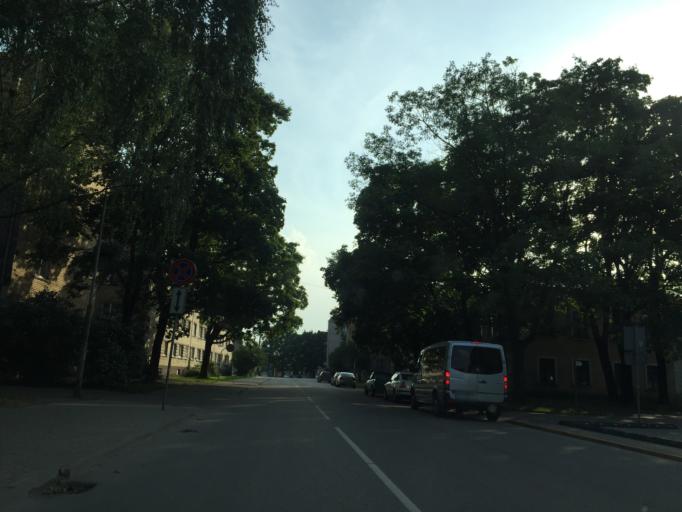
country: LV
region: Jelgava
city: Jelgava
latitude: 56.6534
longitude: 23.7237
